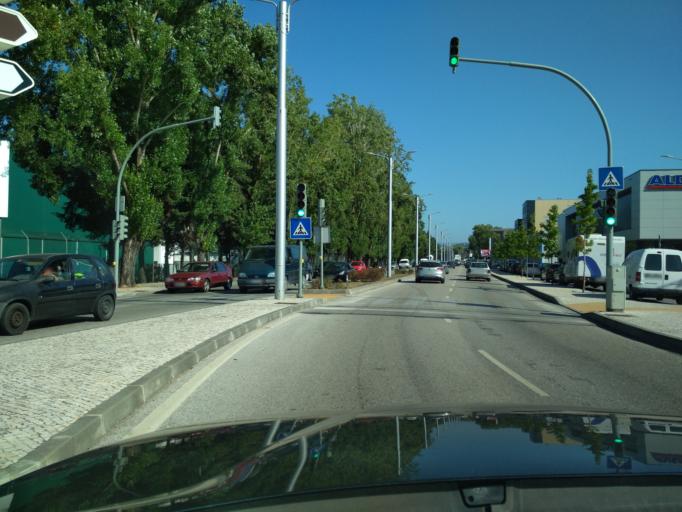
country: PT
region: Coimbra
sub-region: Coimbra
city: Coimbra
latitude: 40.2067
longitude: -8.4373
